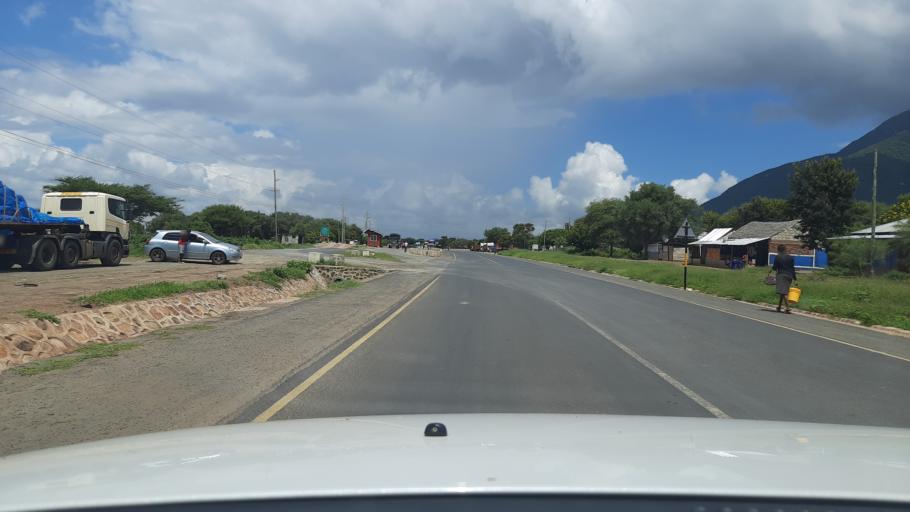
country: TZ
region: Arusha
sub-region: Longido District
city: Longido
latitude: -2.7359
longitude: 36.6992
